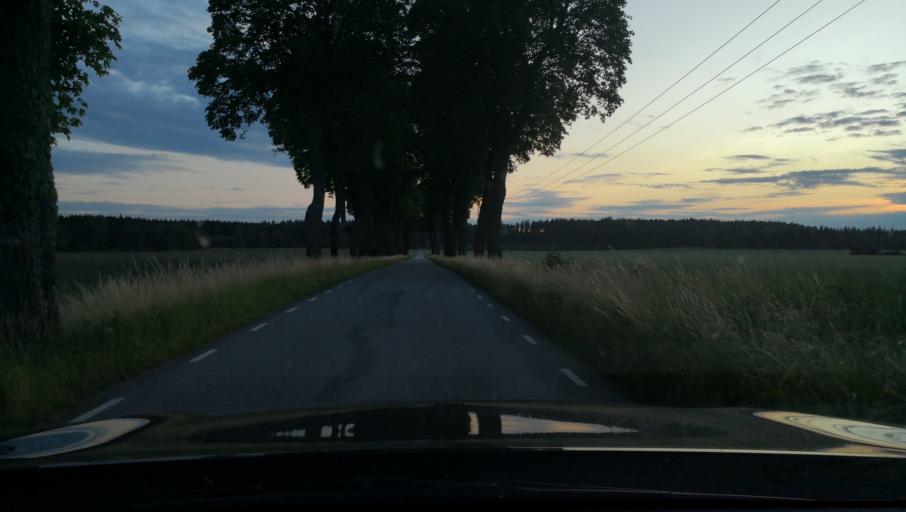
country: SE
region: Uppsala
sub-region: Osthammars Kommun
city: Bjorklinge
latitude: 60.0621
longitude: 17.5569
